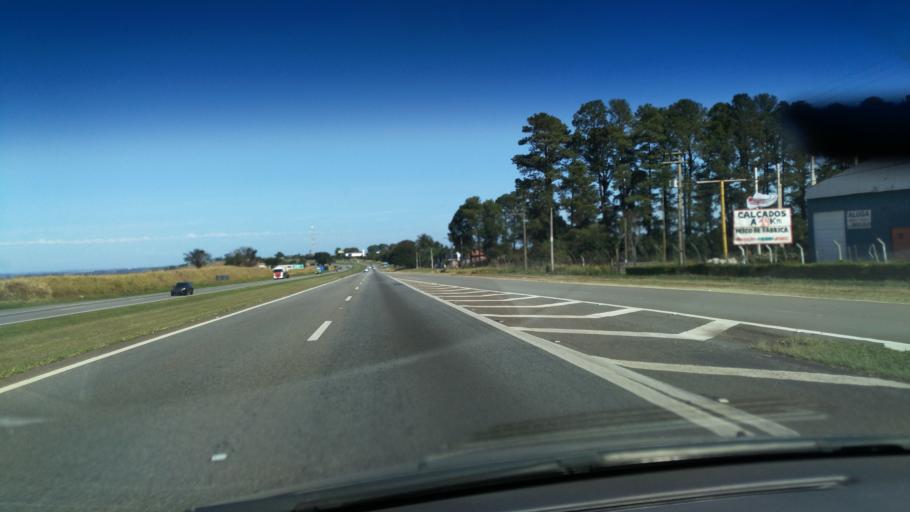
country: BR
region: Sao Paulo
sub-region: Mogi-Mirim
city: Mogi Mirim
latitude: -22.5067
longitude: -46.9873
